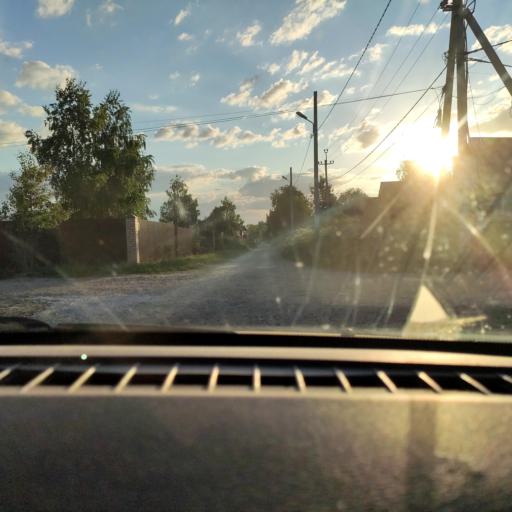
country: RU
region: Perm
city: Polazna
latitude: 58.1289
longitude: 56.4016
